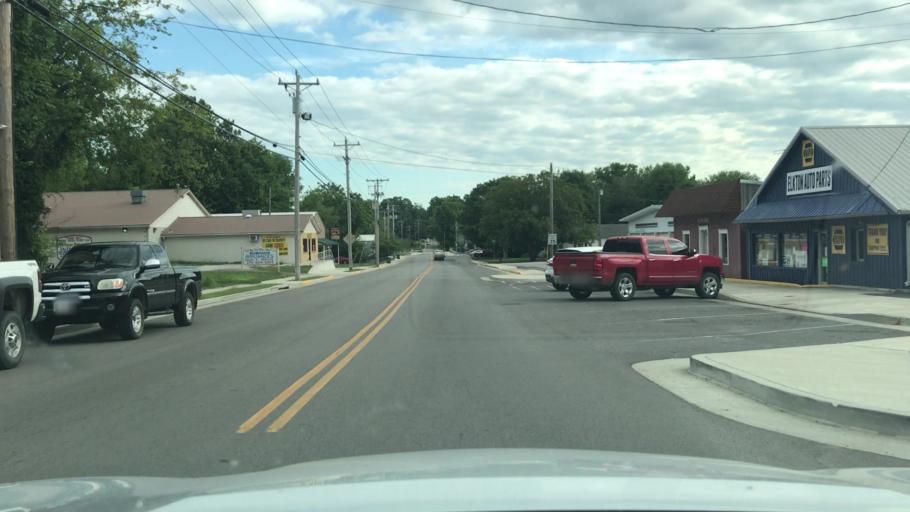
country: US
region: Kentucky
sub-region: Todd County
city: Elkton
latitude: 36.8106
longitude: -87.1538
